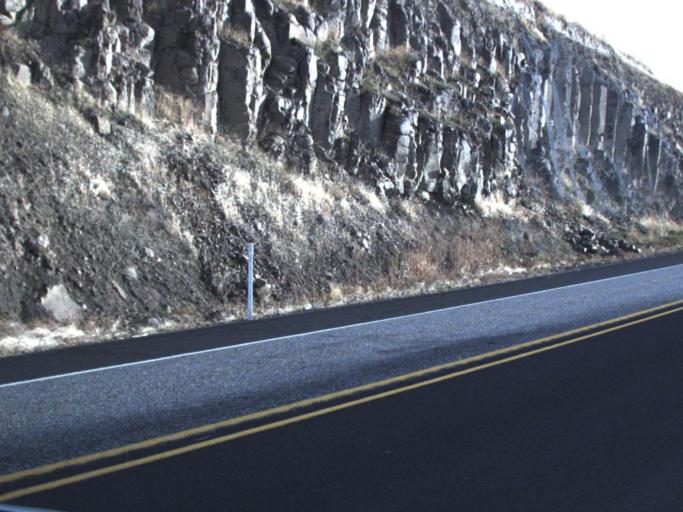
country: US
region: Washington
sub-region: Columbia County
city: Dayton
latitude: 46.4238
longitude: -117.9480
